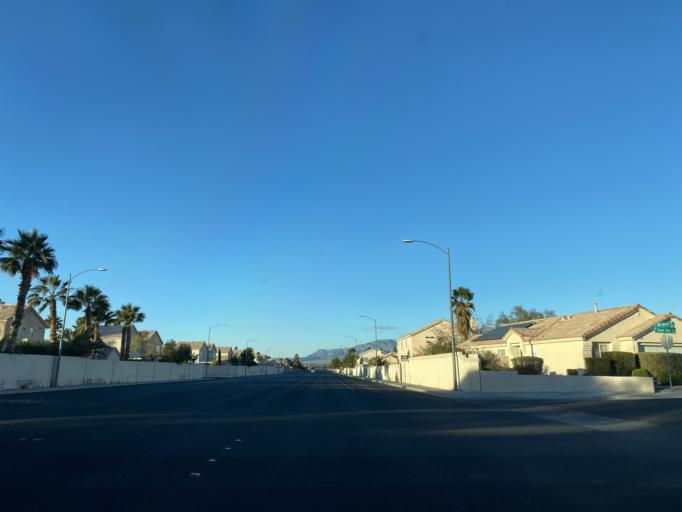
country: US
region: Nevada
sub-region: Clark County
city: Summerlin South
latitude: 36.2231
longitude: -115.2973
